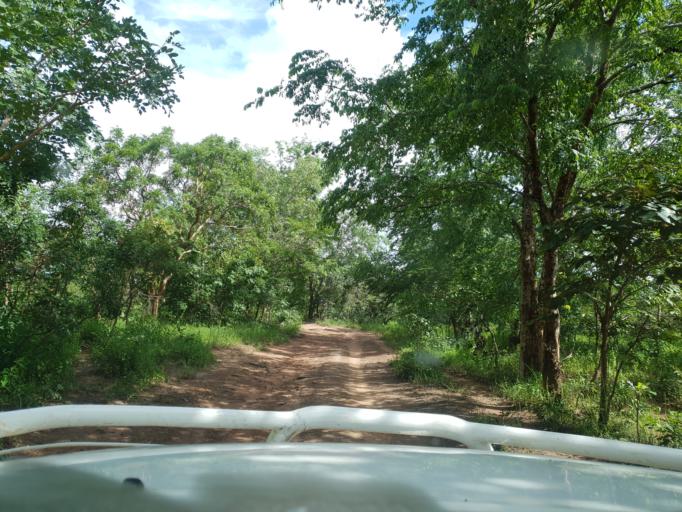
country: CI
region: Savanes
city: Tengrela
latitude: 10.4596
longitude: -6.7960
